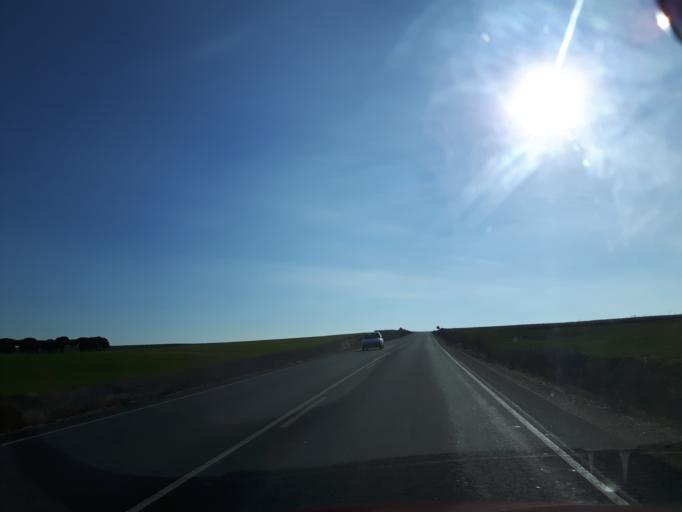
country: ES
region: Castille and Leon
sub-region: Provincia de Salamanca
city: San Cristobal de la Cuesta
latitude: 41.0221
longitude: -5.6254
